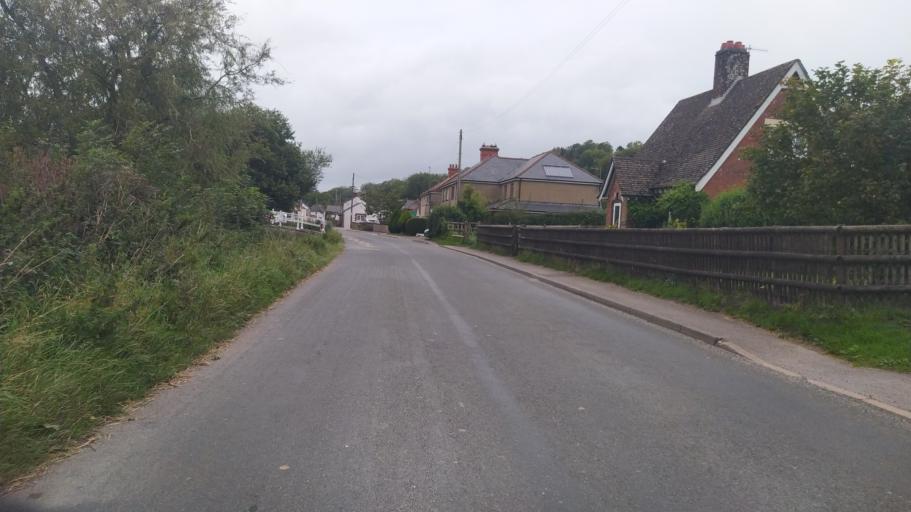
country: GB
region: England
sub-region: Dorset
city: Dorchester
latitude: 50.7935
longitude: -2.4162
